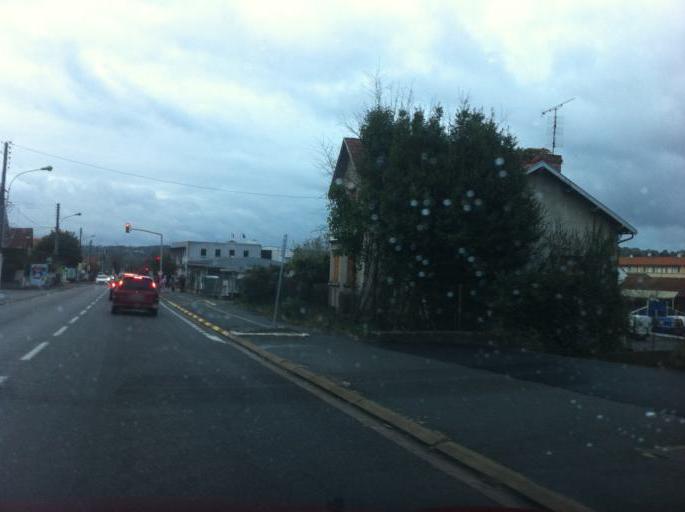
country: FR
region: Aquitaine
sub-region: Departement de la Dordogne
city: Perigueux
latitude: 45.1899
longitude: 0.6961
